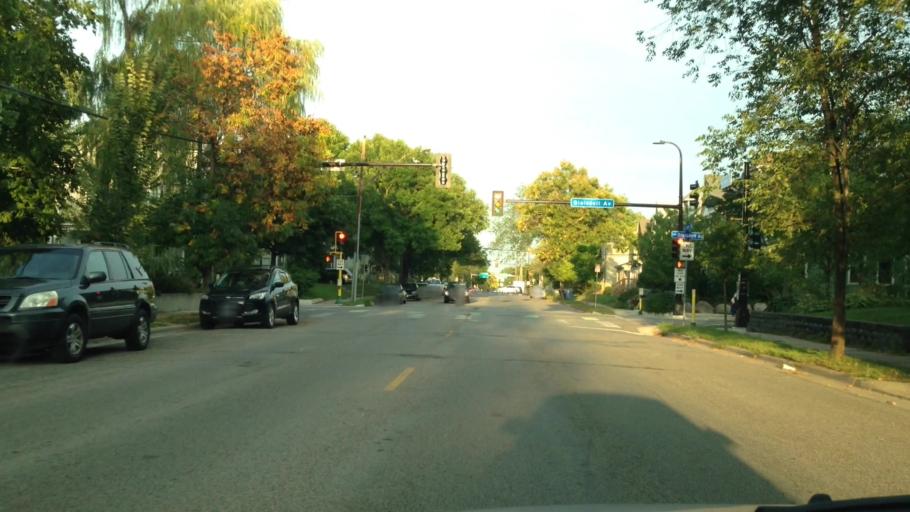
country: US
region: Minnesota
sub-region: Hennepin County
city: Minneapolis
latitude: 44.9377
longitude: -93.2803
